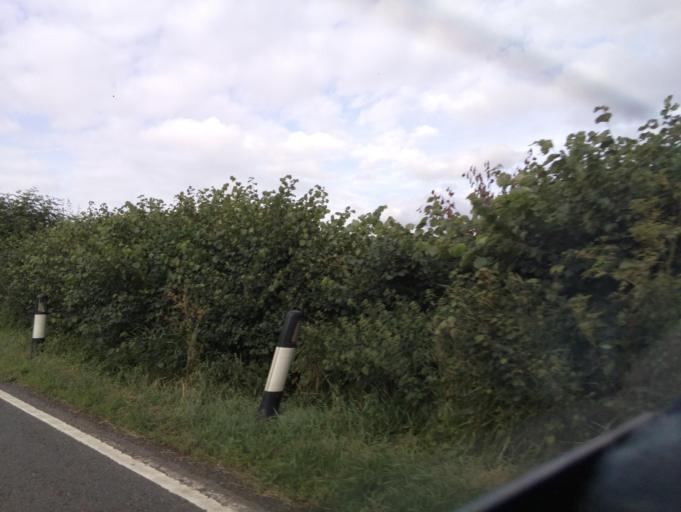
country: GB
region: England
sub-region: Warwickshire
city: Dunchurch
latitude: 52.3062
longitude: -1.3115
